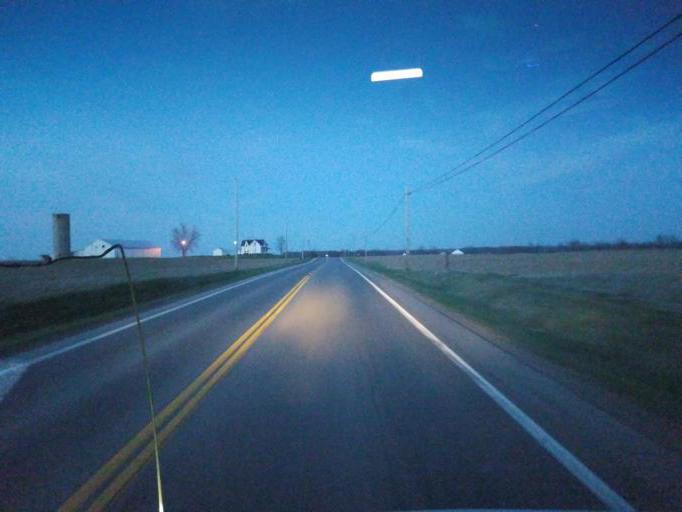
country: US
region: Ohio
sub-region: Logan County
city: De Graff
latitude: 40.3517
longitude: -83.9050
